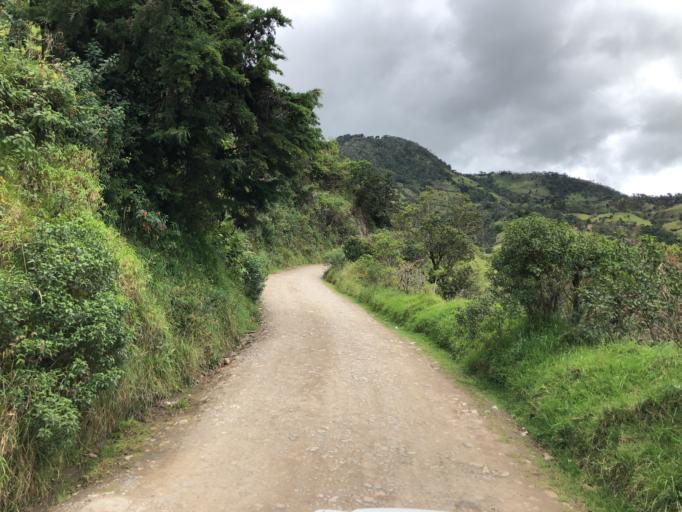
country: CO
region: Cauca
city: Totoro
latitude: 2.5110
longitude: -76.3695
